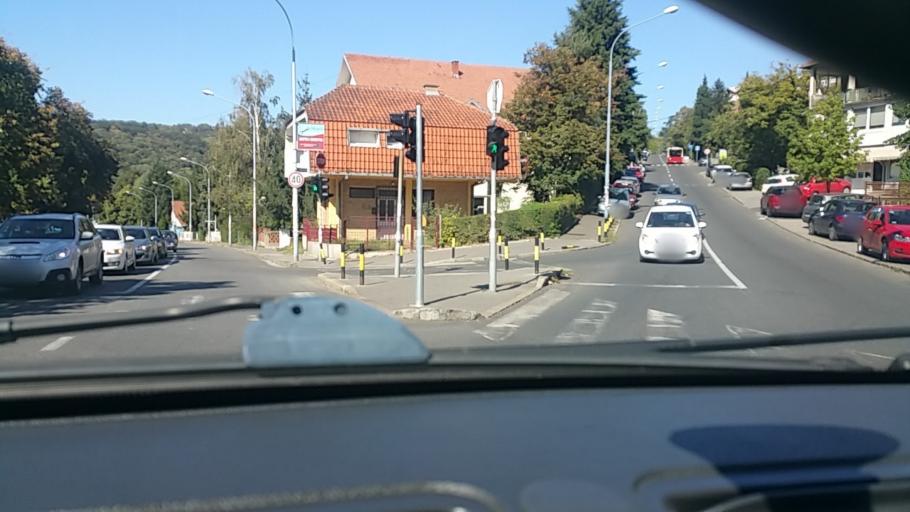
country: RS
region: Central Serbia
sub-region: Belgrade
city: Rakovica
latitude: 44.7504
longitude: 20.4527
